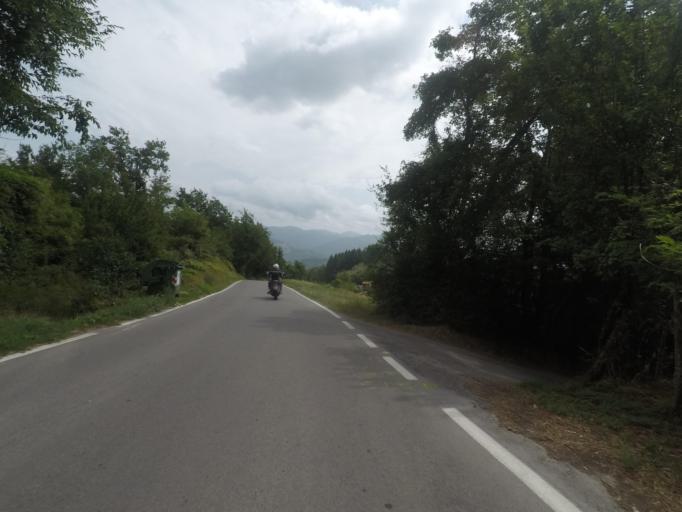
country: IT
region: Tuscany
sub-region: Provincia di Lucca
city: Castelnuovo di Garfagnana
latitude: 44.1122
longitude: 10.3834
